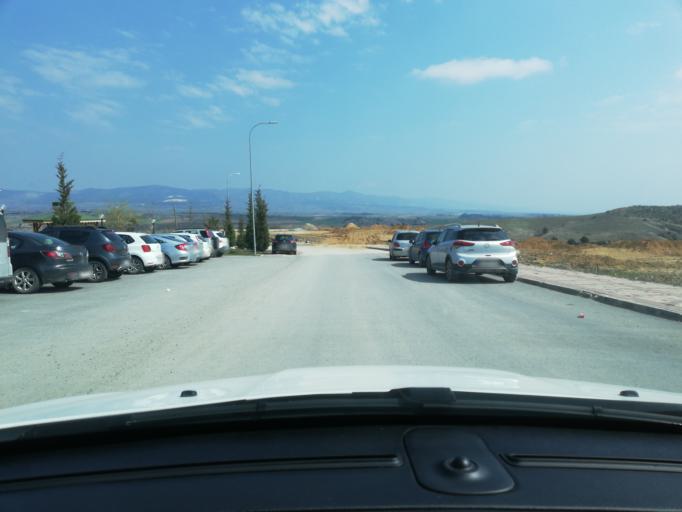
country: TR
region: Kastamonu
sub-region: Cide
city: Kastamonu
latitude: 41.4369
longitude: 33.7667
